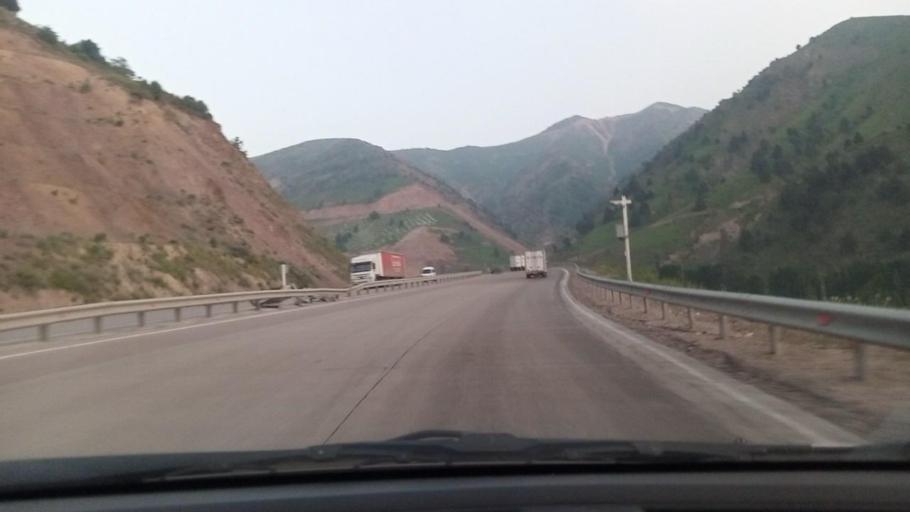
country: UZ
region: Toshkent
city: Angren
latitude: 41.1145
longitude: 70.4969
